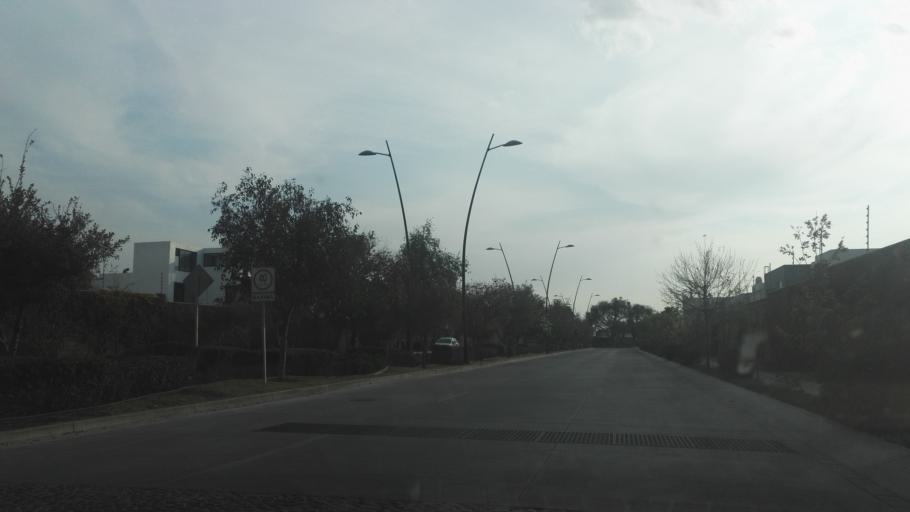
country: MX
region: Guanajuato
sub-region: Leon
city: Ladrilleras del Refugio
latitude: 21.0667
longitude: -101.5969
